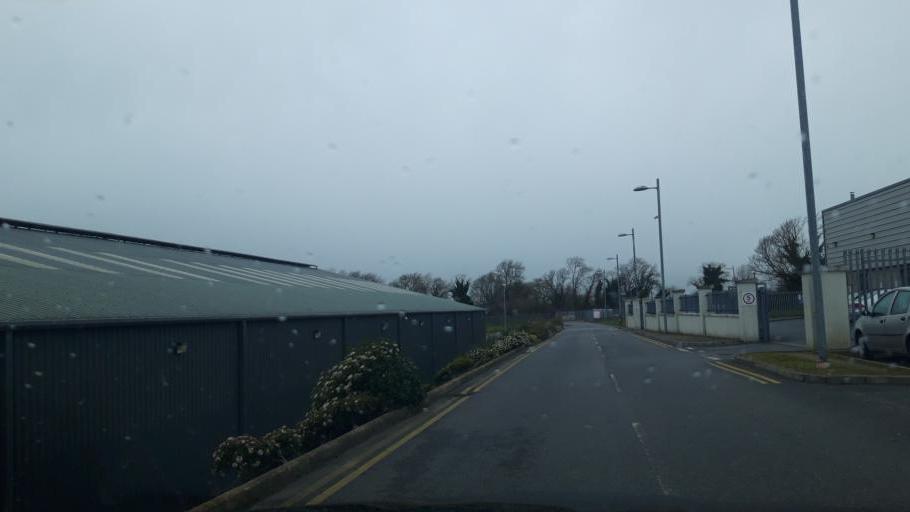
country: IE
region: Leinster
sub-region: Kilkenny
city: Kilkenny
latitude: 52.6514
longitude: -7.2102
